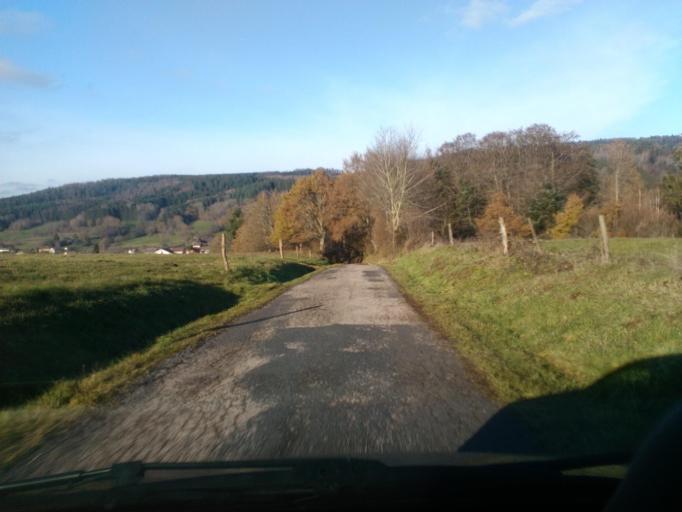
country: FR
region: Lorraine
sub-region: Departement des Vosges
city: Saint-Die-des-Vosges
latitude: 48.3372
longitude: 6.9668
